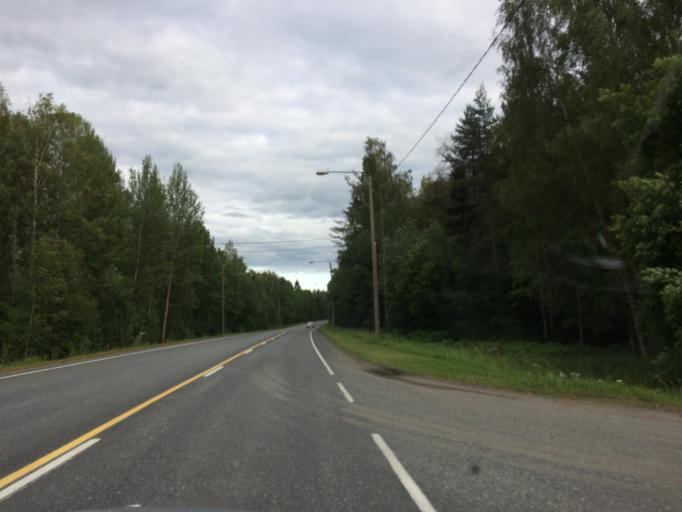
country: FI
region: Haeme
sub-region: Haemeenlinna
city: Haemeenlinna
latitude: 60.9482
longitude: 24.5101
